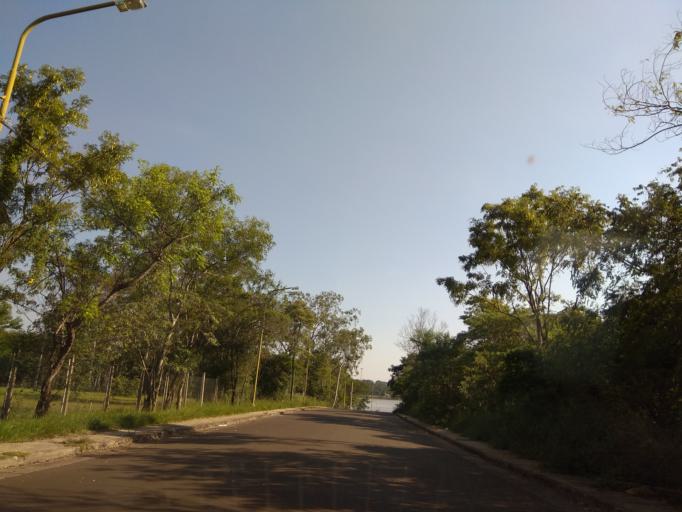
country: AR
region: Misiones
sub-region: Departamento de Capital
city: Posadas
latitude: -27.3548
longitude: -55.9414
